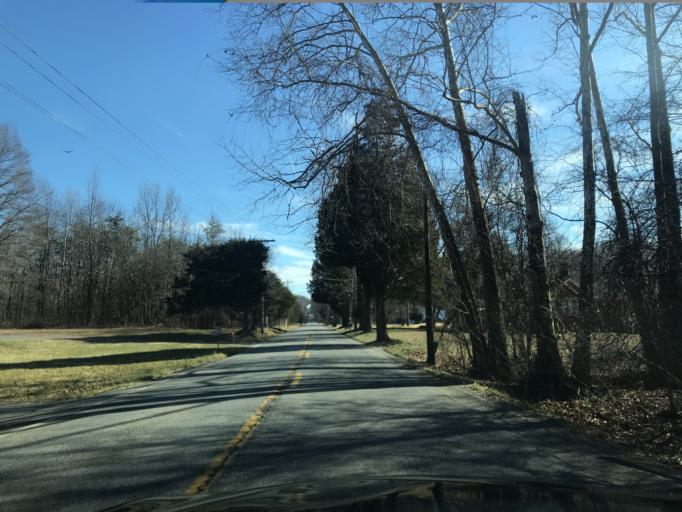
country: US
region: Maryland
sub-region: Charles County
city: Bryans Road
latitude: 38.5911
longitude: -77.0516
